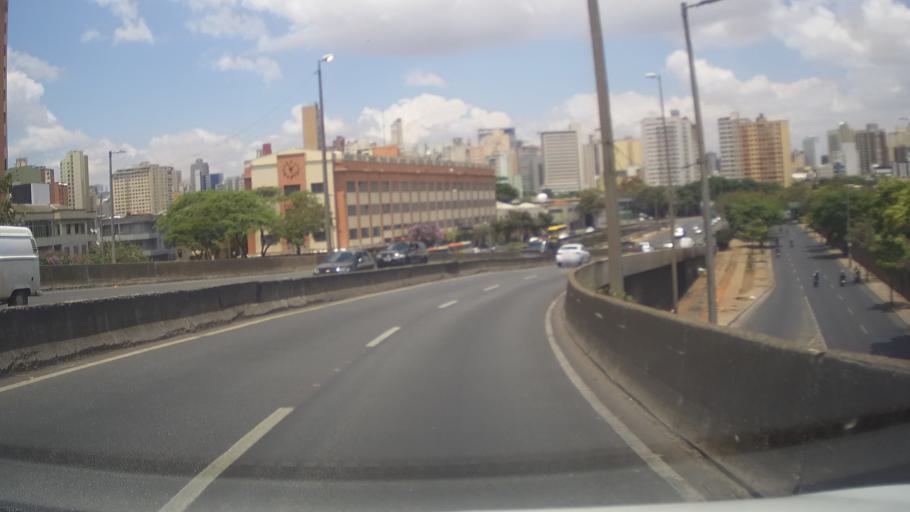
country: BR
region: Minas Gerais
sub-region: Belo Horizonte
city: Belo Horizonte
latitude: -19.9152
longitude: -43.9449
